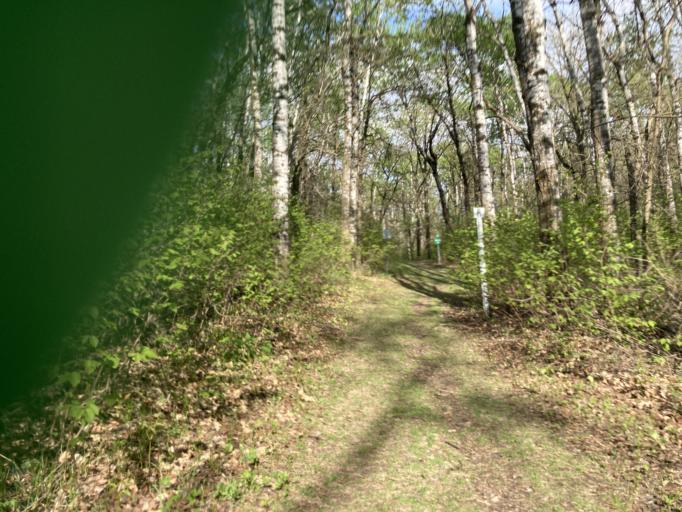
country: CA
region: Manitoba
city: Brandon
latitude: 49.7178
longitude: -99.9017
